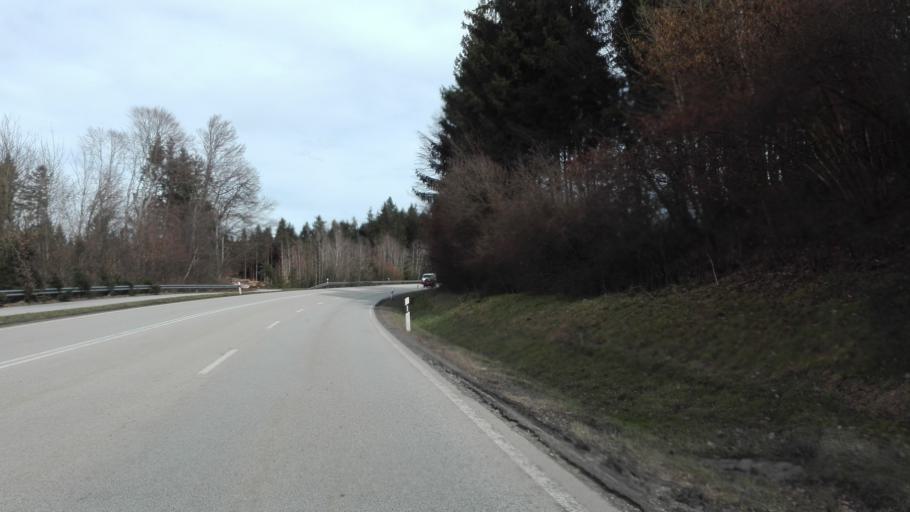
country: DE
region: Bavaria
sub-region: Lower Bavaria
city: Thyrnau
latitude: 48.5998
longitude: 13.5197
